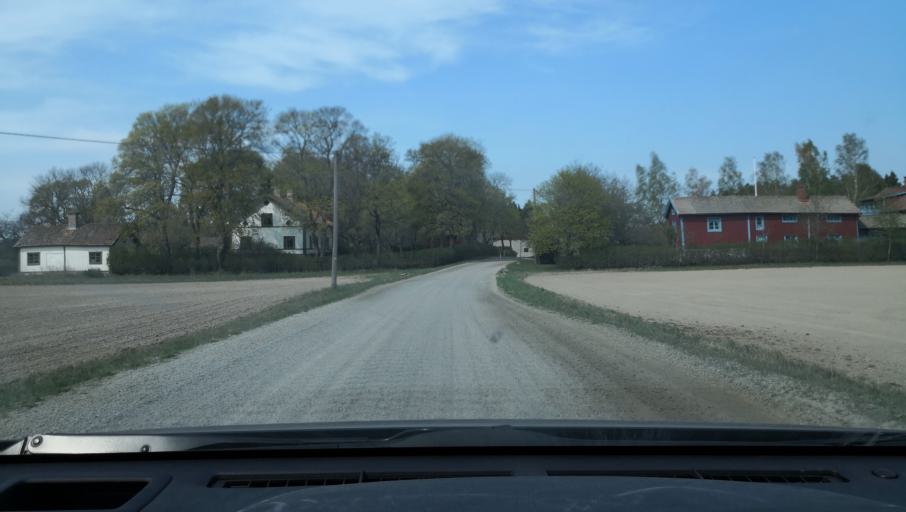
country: SE
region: Vaestmanland
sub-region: Vasteras
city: Skultuna
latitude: 59.7846
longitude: 16.4589
